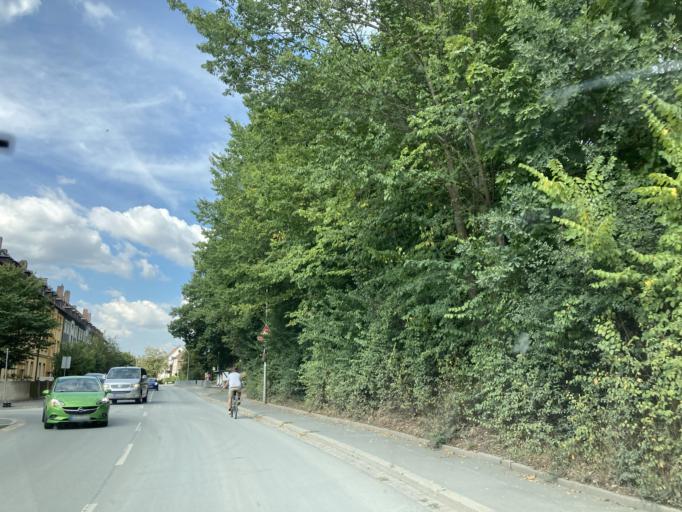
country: DE
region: Bavaria
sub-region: Upper Franconia
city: Kulmbach
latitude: 50.1160
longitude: 11.4667
